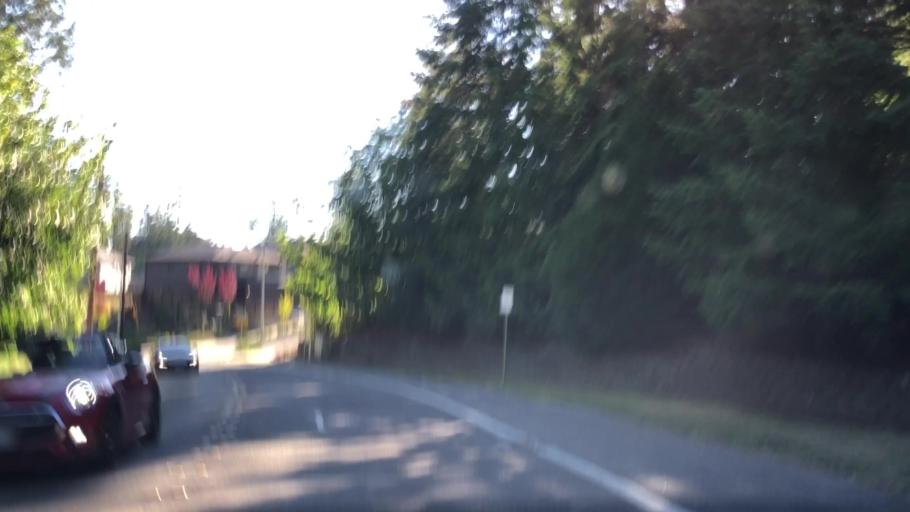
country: US
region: Washington
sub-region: Snohomish County
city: Martha Lake
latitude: 47.8316
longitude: -122.2507
